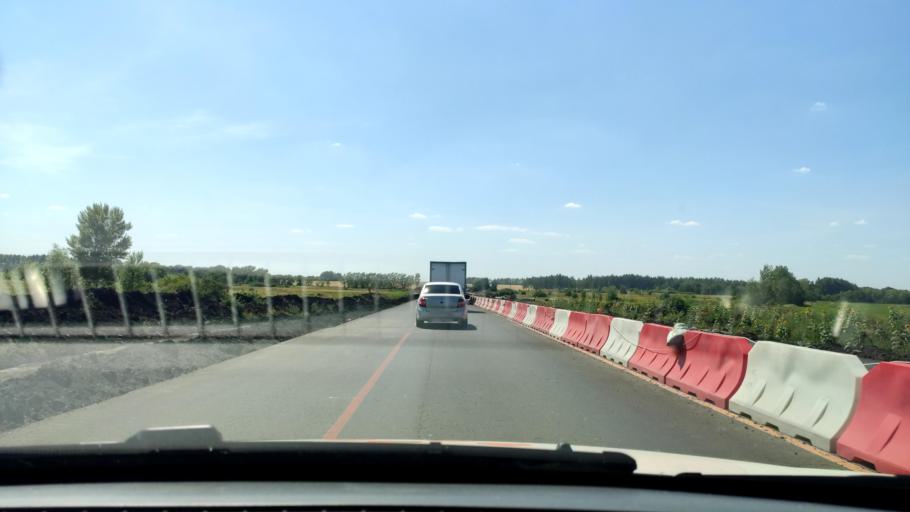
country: RU
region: Voronezj
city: Pereleshino
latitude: 51.7146
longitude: 40.0108
